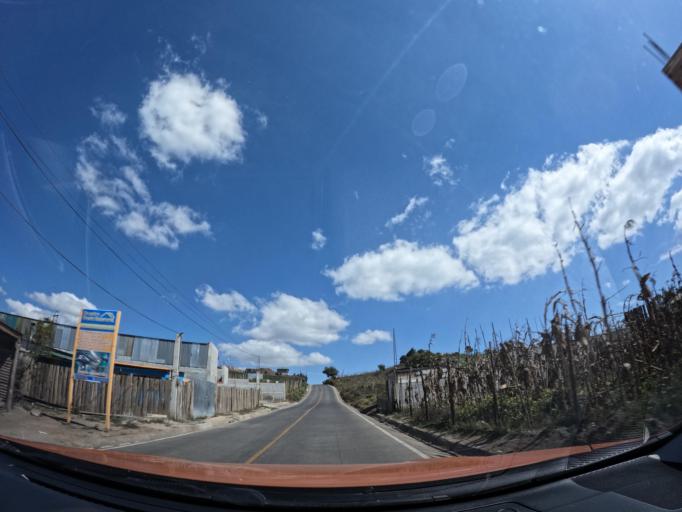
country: GT
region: Chimaltenango
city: Patzun
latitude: 14.6542
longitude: -91.0537
